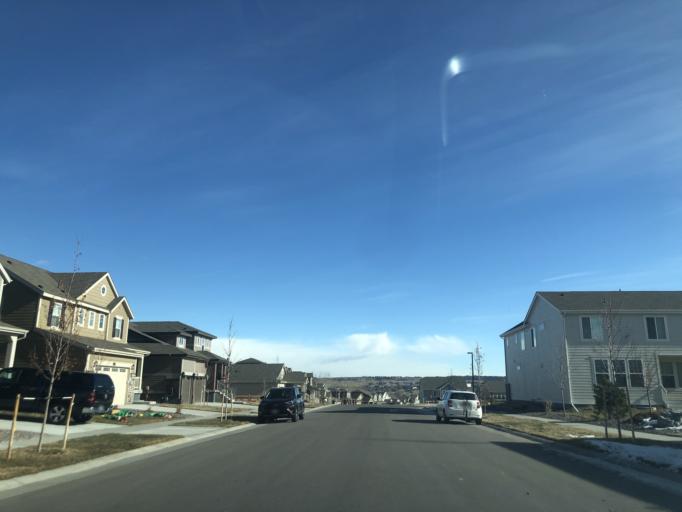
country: US
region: Colorado
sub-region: Douglas County
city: Stonegate
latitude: 39.5582
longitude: -104.8058
